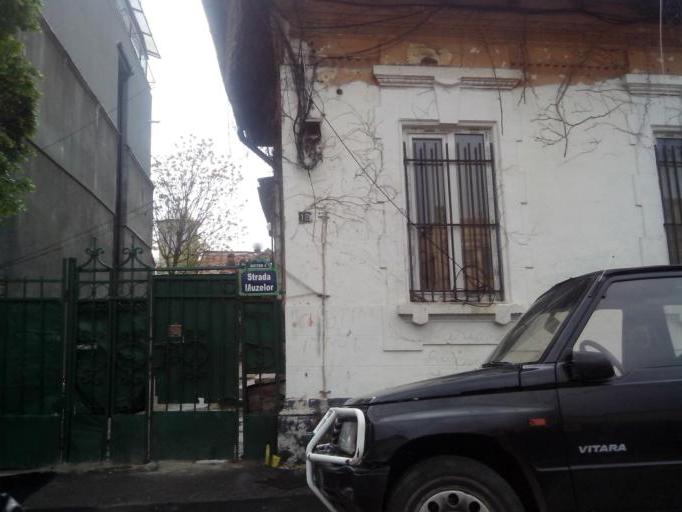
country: RO
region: Bucuresti
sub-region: Municipiul Bucuresti
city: Bucuresti
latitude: 44.4217
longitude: 26.1001
